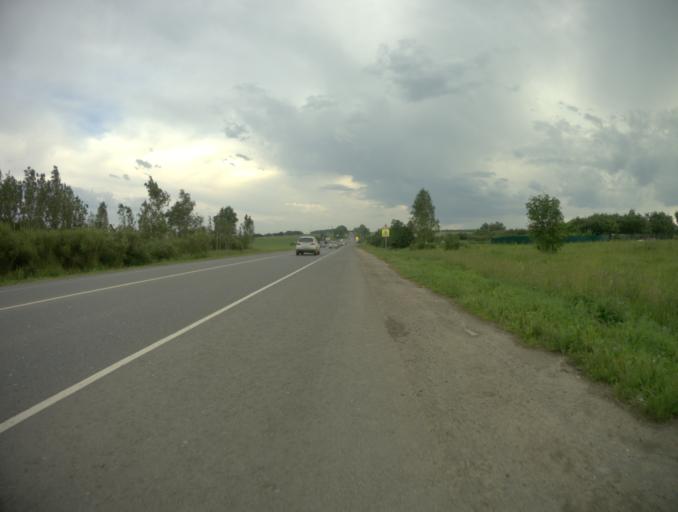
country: RU
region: Vladimir
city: Bogolyubovo
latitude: 56.1957
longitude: 40.4465
